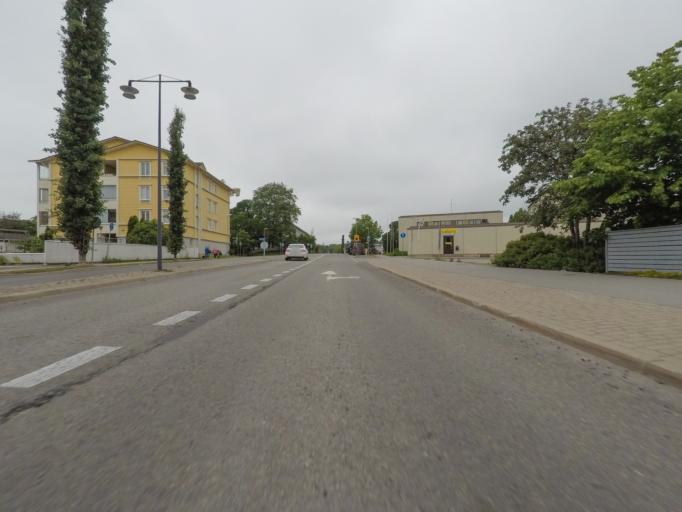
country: FI
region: Varsinais-Suomi
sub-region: Turku
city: Naantali
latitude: 60.4674
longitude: 22.0298
